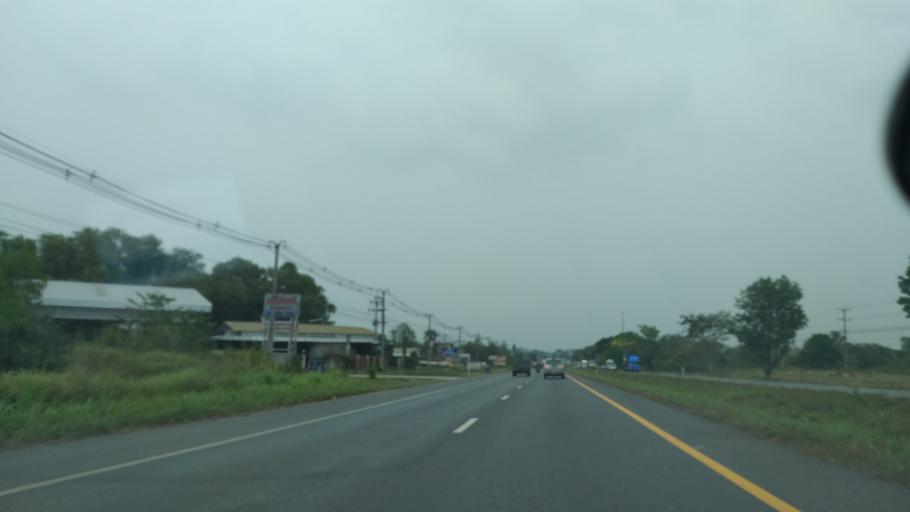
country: TH
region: Chon Buri
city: Ko Chan
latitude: 13.3102
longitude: 101.2653
